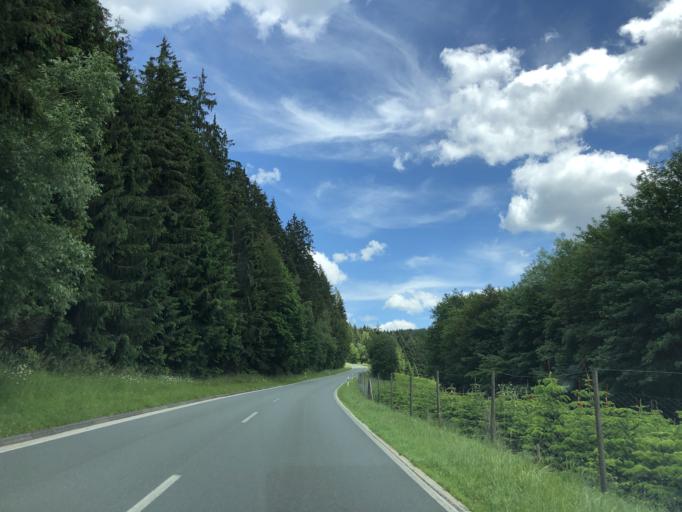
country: DE
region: North Rhine-Westphalia
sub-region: Regierungsbezirk Arnsberg
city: Kirchhundem
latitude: 51.0933
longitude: 8.1247
